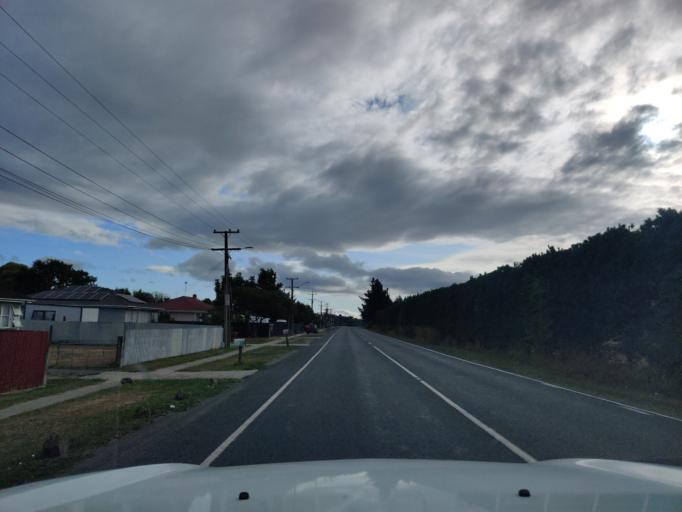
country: NZ
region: Waikato
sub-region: Waipa District
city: Cambridge
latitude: -37.7832
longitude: 175.4234
